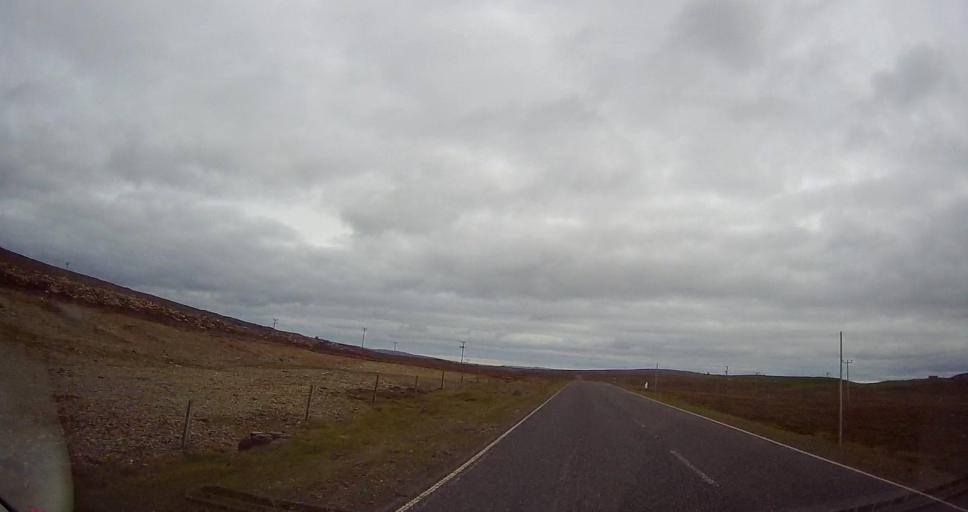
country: GB
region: Scotland
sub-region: Shetland Islands
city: Shetland
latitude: 60.7217
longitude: -0.9096
